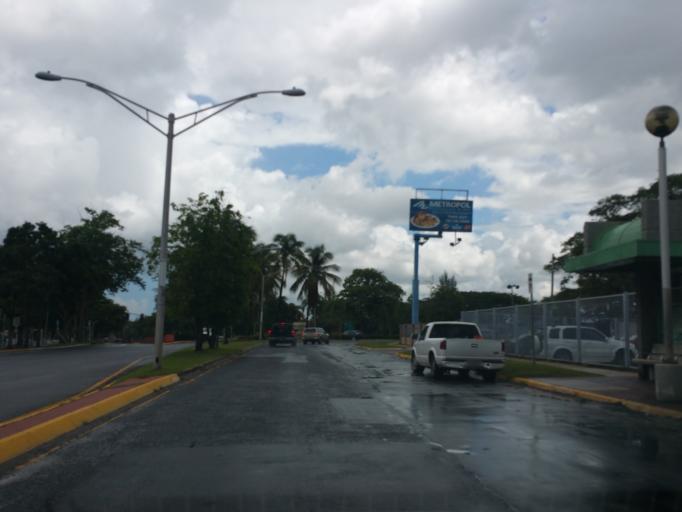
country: PR
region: Carolina
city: Carolina
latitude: 18.4420
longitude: -66.0154
